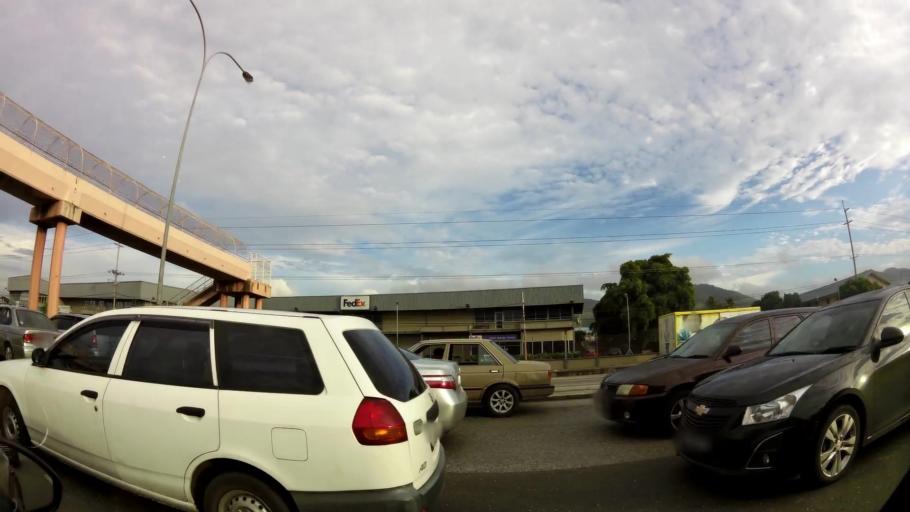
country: TT
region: Tunapuna/Piarco
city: Tunapuna
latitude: 10.6375
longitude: -61.3895
